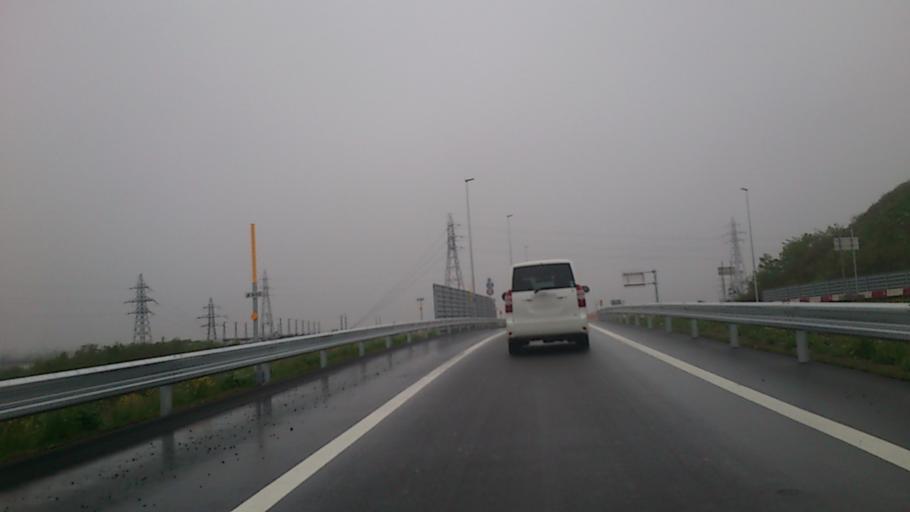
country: JP
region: Hokkaido
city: Kushiro
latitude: 43.0035
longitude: 144.4311
